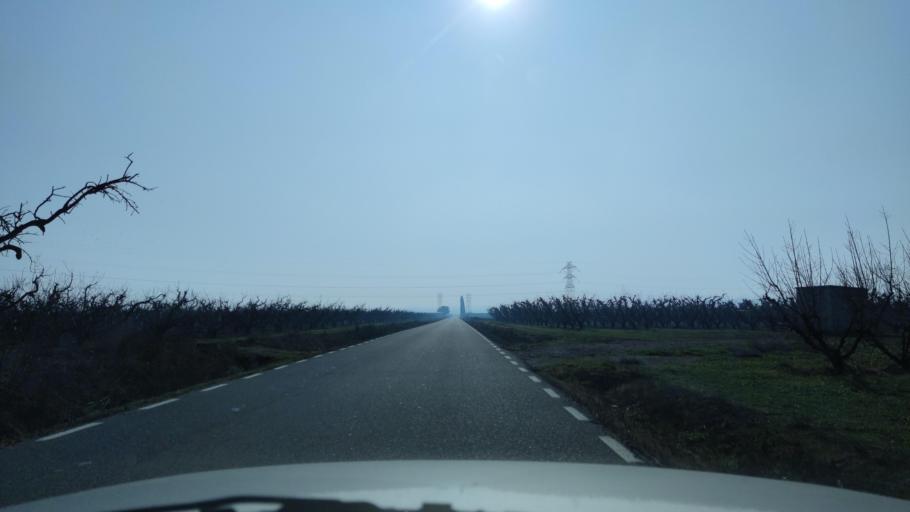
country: ES
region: Catalonia
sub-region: Provincia de Lleida
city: Sunyer
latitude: 41.5525
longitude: 0.5736
